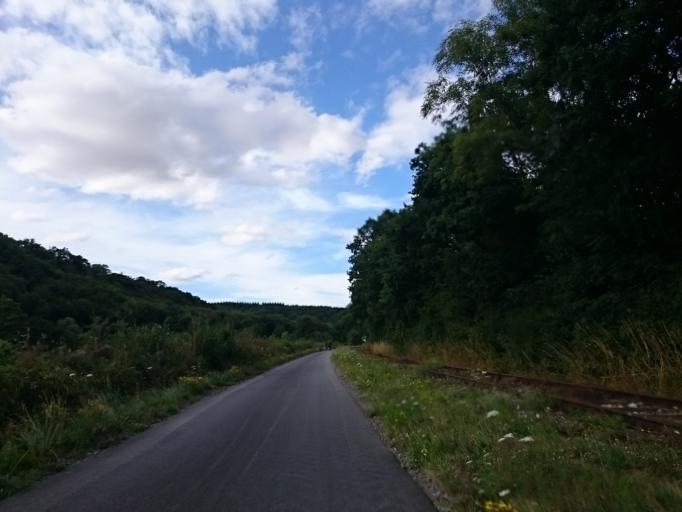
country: FR
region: Lower Normandy
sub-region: Departement du Calvados
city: Sainte-Honorine-du-Fay
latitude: 49.0591
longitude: -0.4596
